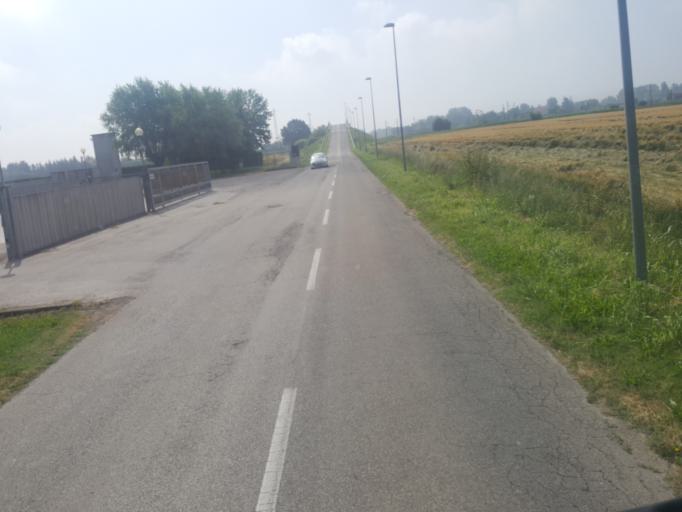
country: IT
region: Veneto
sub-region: Provincia di Rovigo
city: Canaro
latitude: 44.9290
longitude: 11.6828
